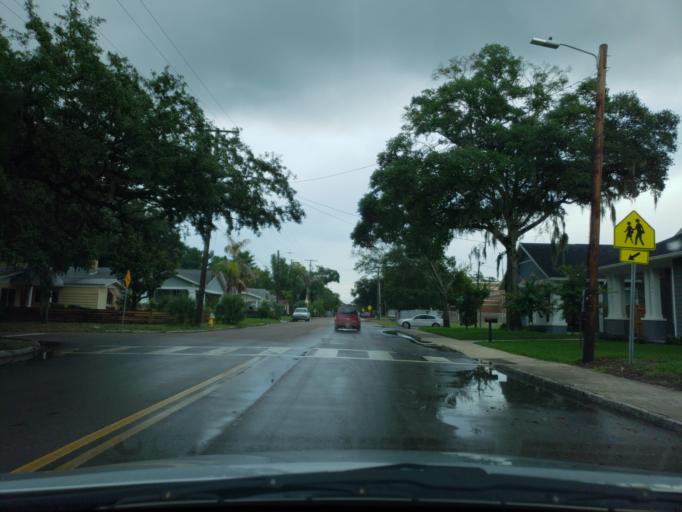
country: US
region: Florida
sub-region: Hillsborough County
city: Tampa
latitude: 27.9888
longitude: -82.4659
